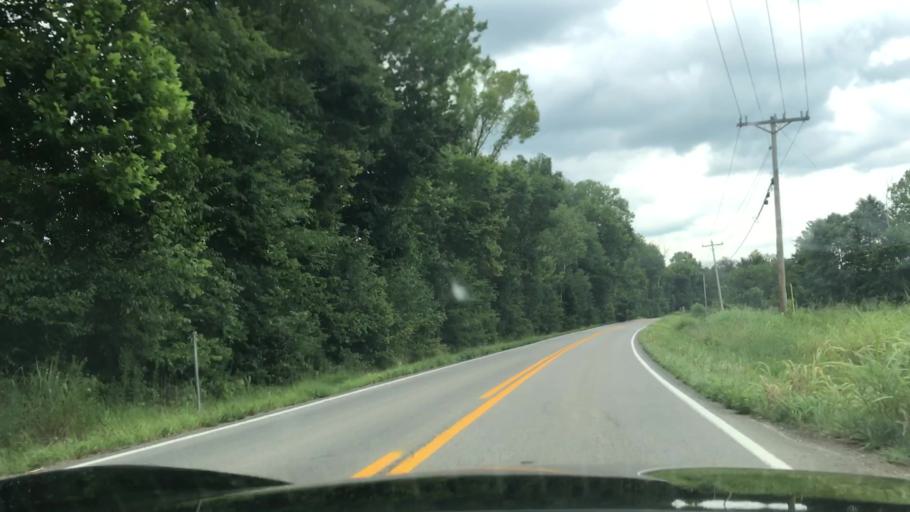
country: US
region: Kentucky
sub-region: Muhlenberg County
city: Central City
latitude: 37.2039
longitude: -87.0223
